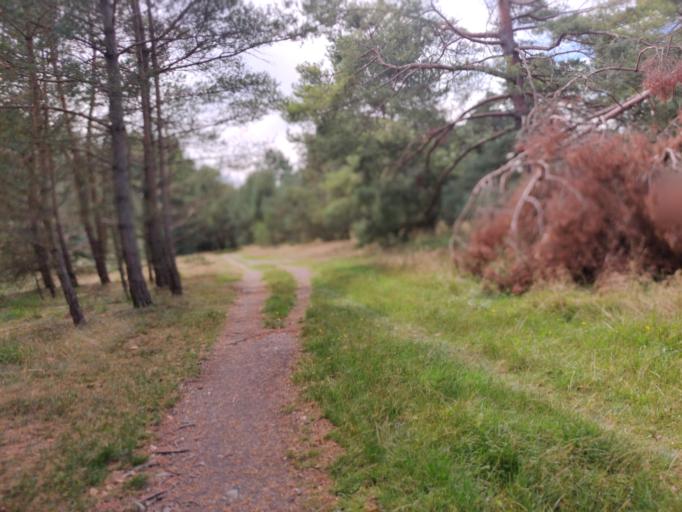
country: DE
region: Lower Saxony
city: Langelsheim
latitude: 51.9607
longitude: 10.3550
